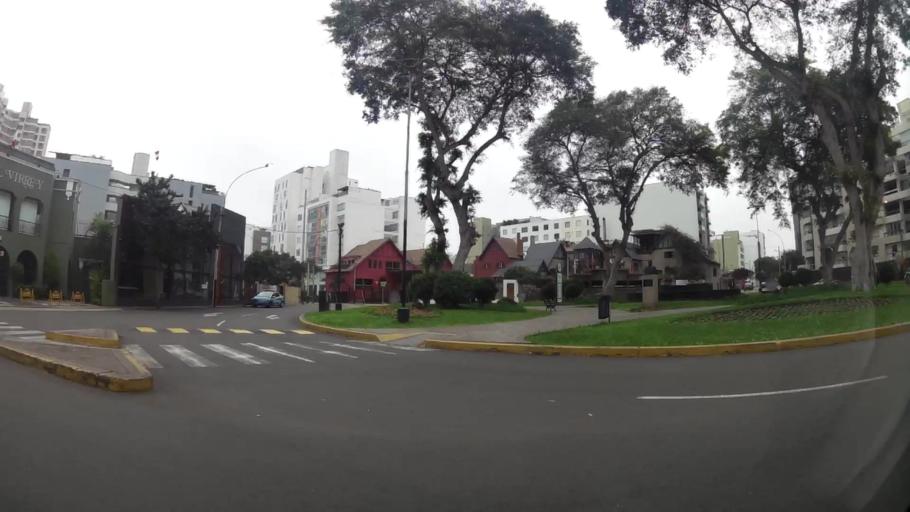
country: PE
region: Lima
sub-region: Lima
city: San Isidro
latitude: -12.1236
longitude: -77.0358
